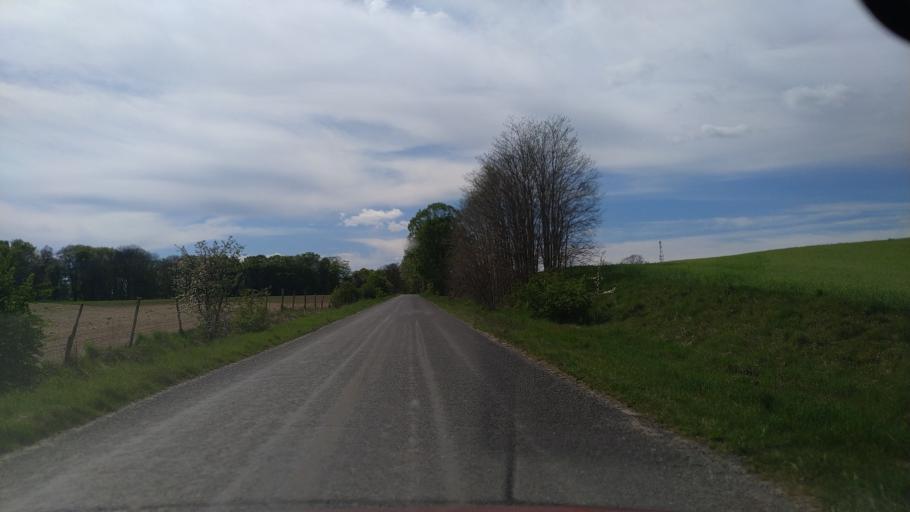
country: PL
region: West Pomeranian Voivodeship
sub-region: Powiat walecki
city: Walcz
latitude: 53.3541
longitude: 16.2950
